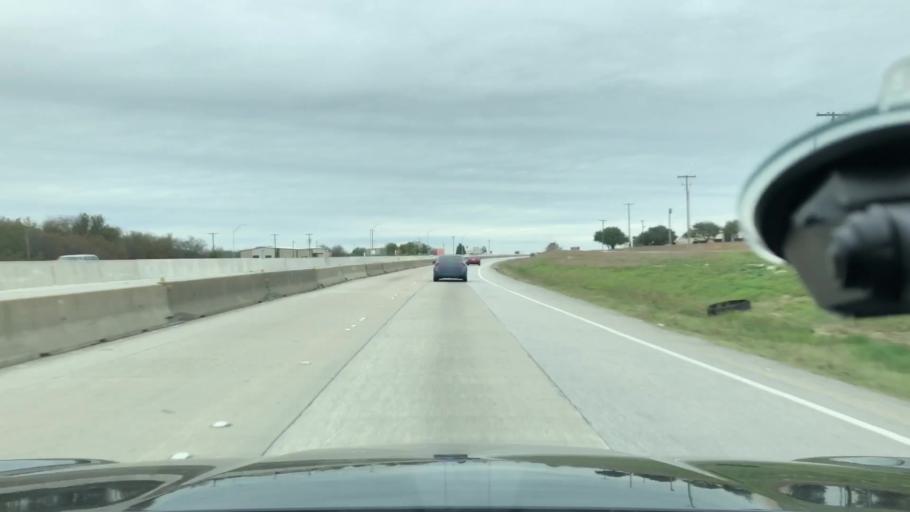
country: US
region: Texas
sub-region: Ellis County
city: Waxahachie
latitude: 32.4144
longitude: -96.8715
